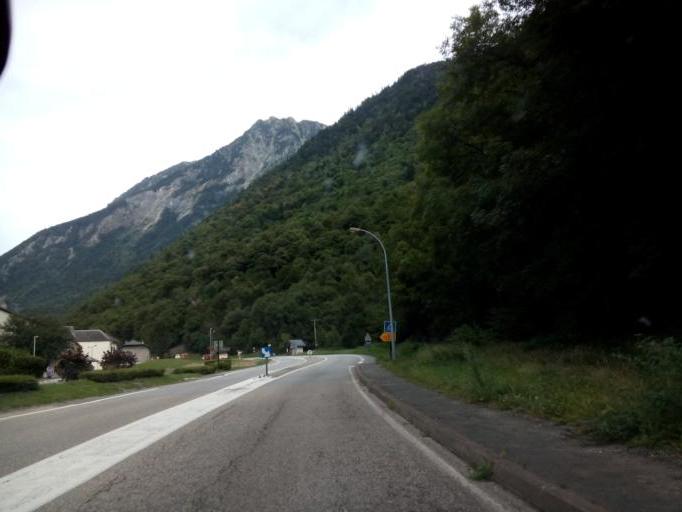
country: FR
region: Rhone-Alpes
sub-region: Departement de l'Isere
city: Vaulnaveys-le-Bas
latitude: 45.0758
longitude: 5.8813
